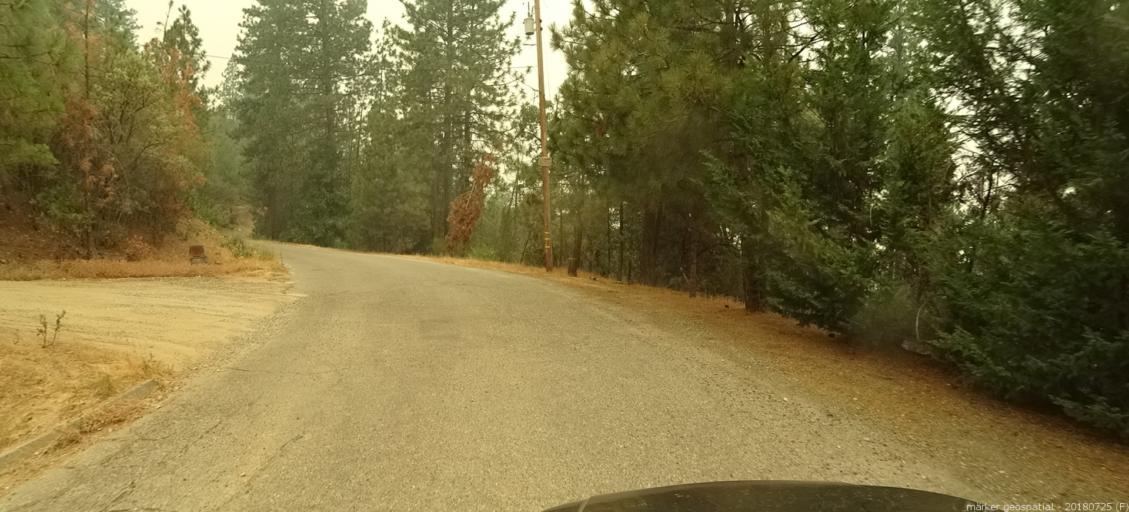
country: US
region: California
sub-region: Madera County
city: Oakhurst
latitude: 37.3590
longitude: -119.6128
